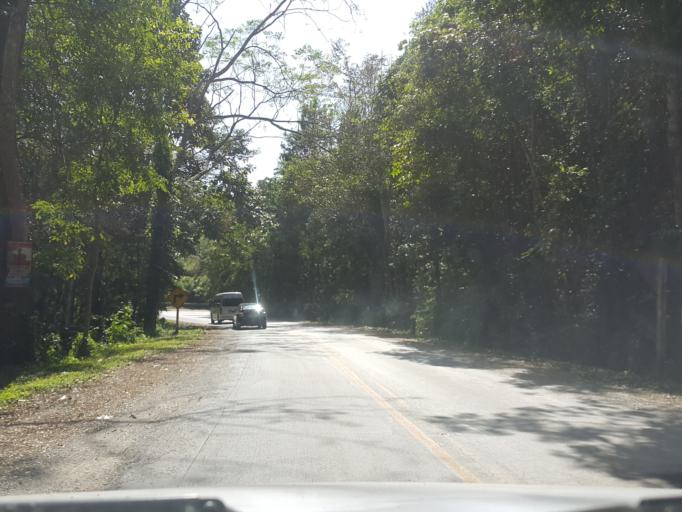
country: TH
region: Chiang Mai
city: Mae Taeng
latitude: 19.1352
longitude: 98.7027
